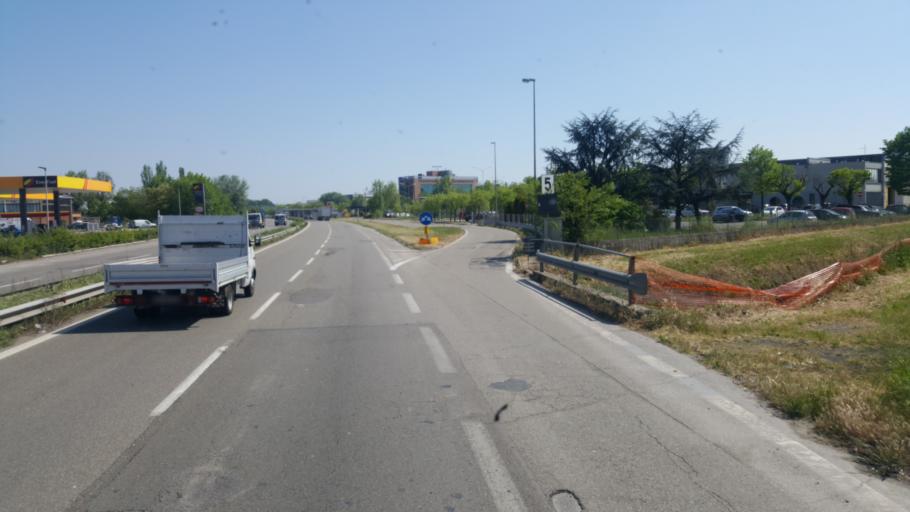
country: IT
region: Emilia-Romagna
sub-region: Provincia di Modena
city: Modena
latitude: 44.6545
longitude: 10.9562
